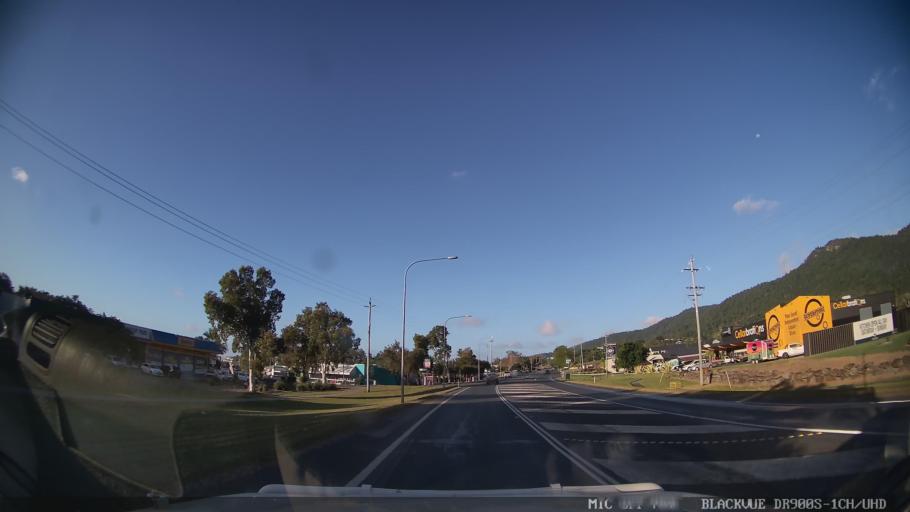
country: AU
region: Queensland
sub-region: Whitsunday
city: Proserpine
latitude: -20.2866
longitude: 148.6800
